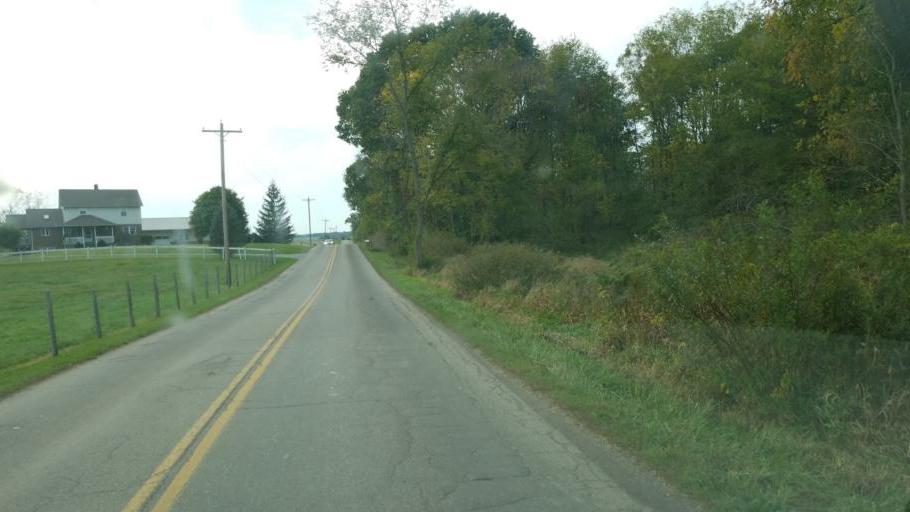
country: US
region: Ohio
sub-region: Holmes County
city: Millersburg
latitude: 40.5872
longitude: -81.8208
